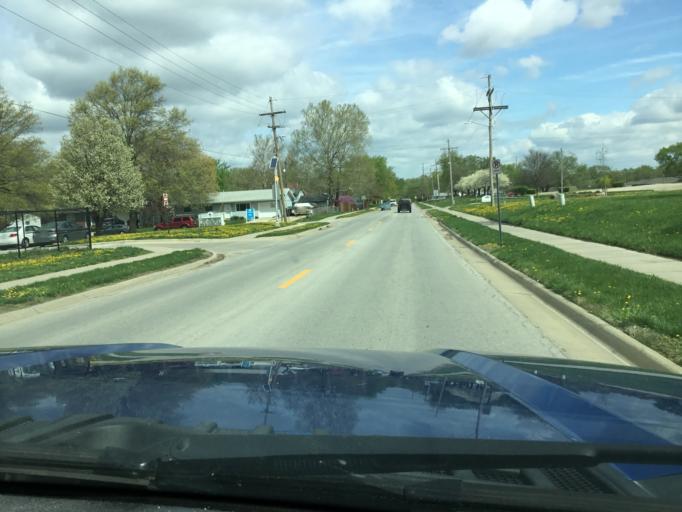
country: US
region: Kansas
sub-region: Douglas County
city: Lawrence
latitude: 38.9469
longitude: -95.2141
